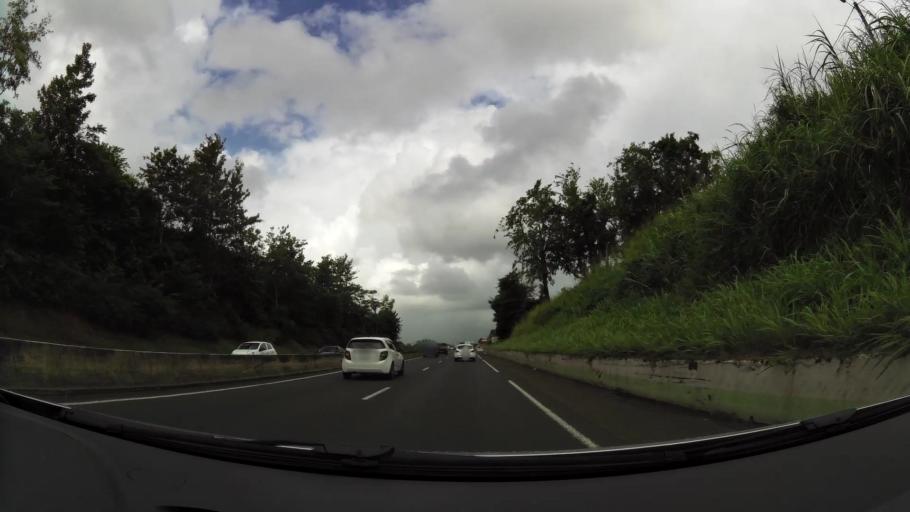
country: MQ
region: Martinique
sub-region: Martinique
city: Ducos
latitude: 14.5868
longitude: -60.9811
